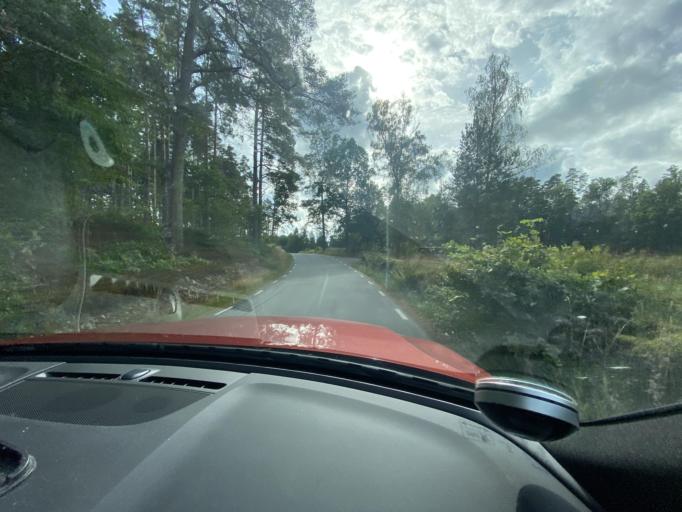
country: SE
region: Skane
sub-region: Hassleholms Kommun
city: Bjarnum
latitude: 56.3596
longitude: 13.8001
